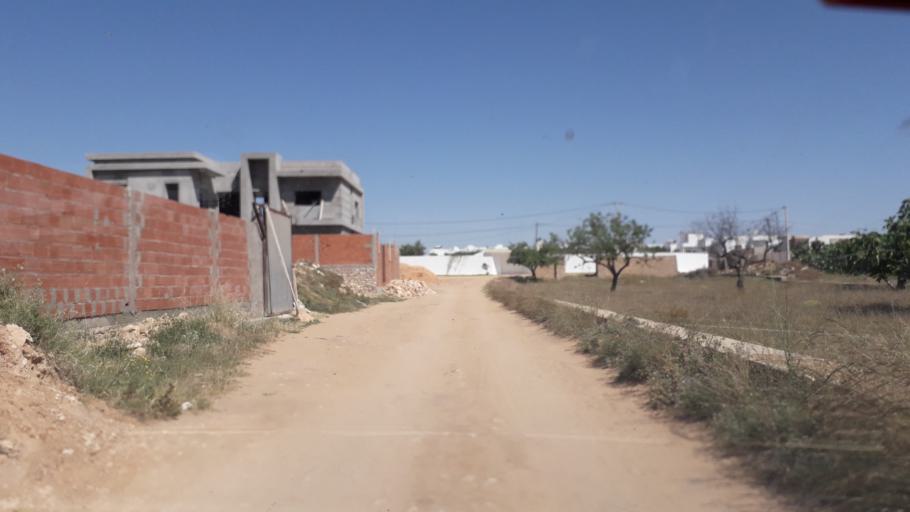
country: TN
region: Safaqis
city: Al Qarmadah
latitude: 34.8029
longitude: 10.7756
